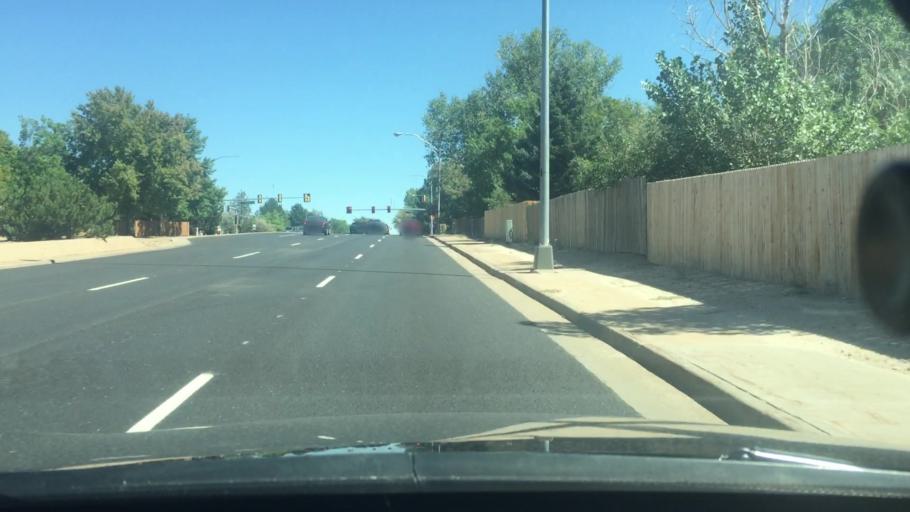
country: US
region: Colorado
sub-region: Arapahoe County
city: Dove Valley
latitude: 39.6384
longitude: -104.8121
